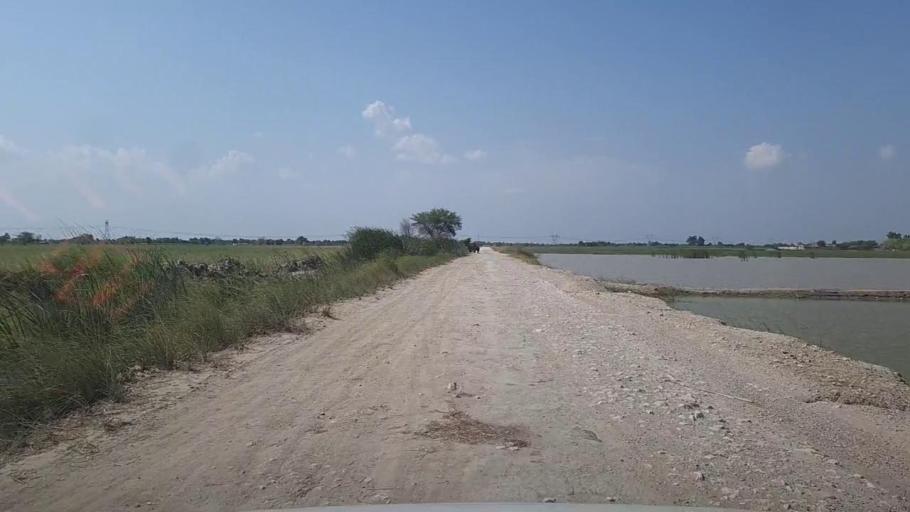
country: PK
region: Sindh
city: Khairpur
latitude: 28.0990
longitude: 69.6266
